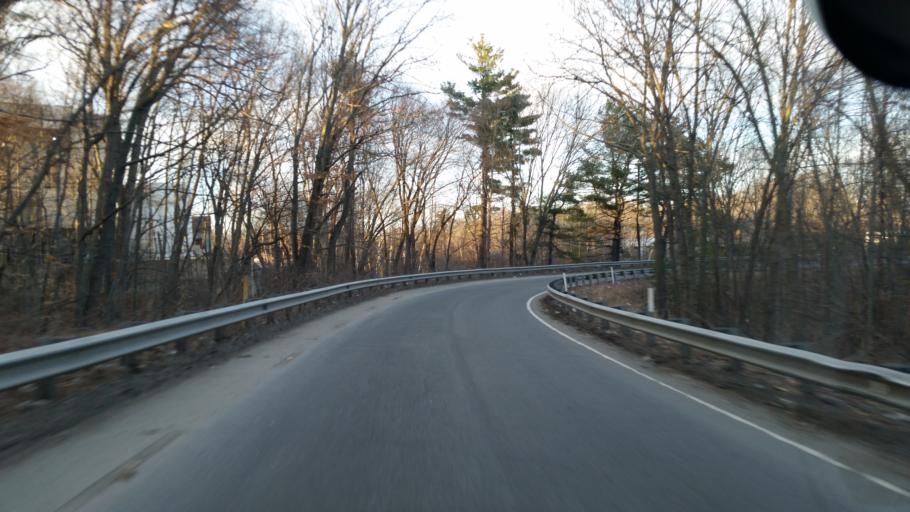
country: US
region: Massachusetts
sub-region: Essex County
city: Haverhill
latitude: 42.7638
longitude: -71.1237
